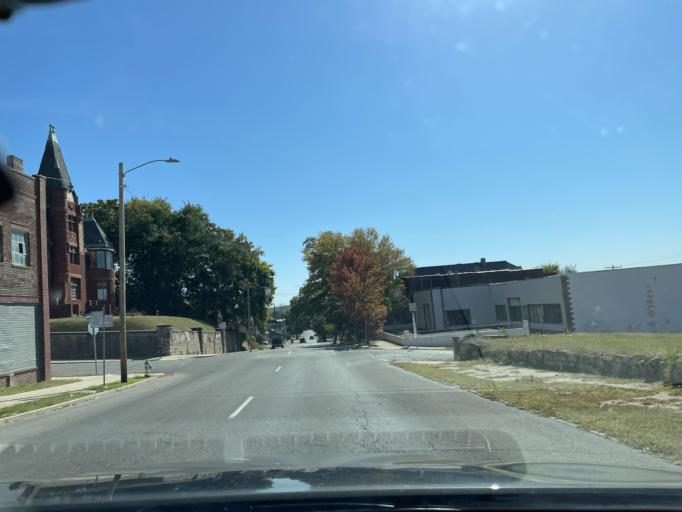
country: US
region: Missouri
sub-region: Buchanan County
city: Saint Joseph
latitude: 39.7645
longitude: -94.8494
